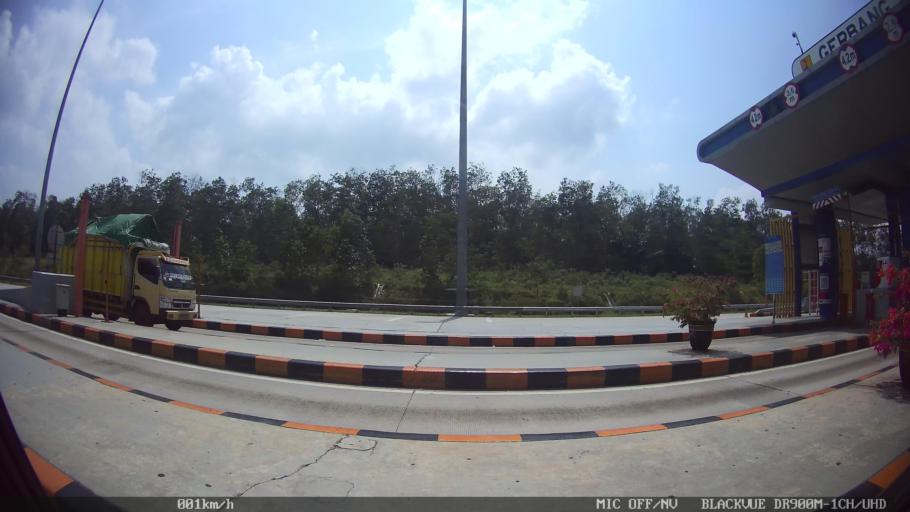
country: ID
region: Lampung
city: Kedaton
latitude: -5.3586
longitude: 105.3272
